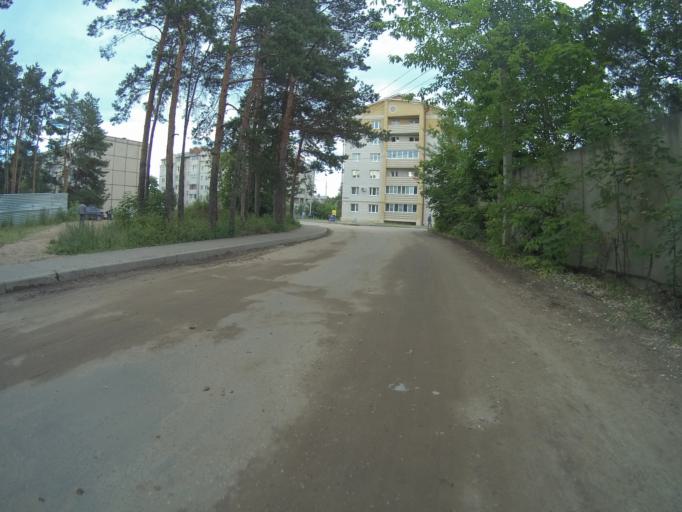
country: RU
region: Vladimir
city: Kommunar
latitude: 56.1044
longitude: 40.4417
